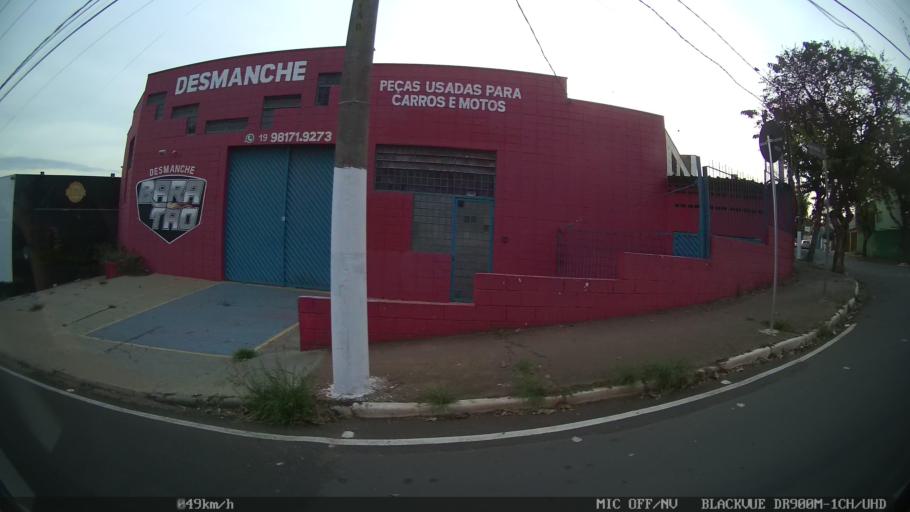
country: BR
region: Sao Paulo
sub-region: Limeira
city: Limeira
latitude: -22.5810
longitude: -47.4091
